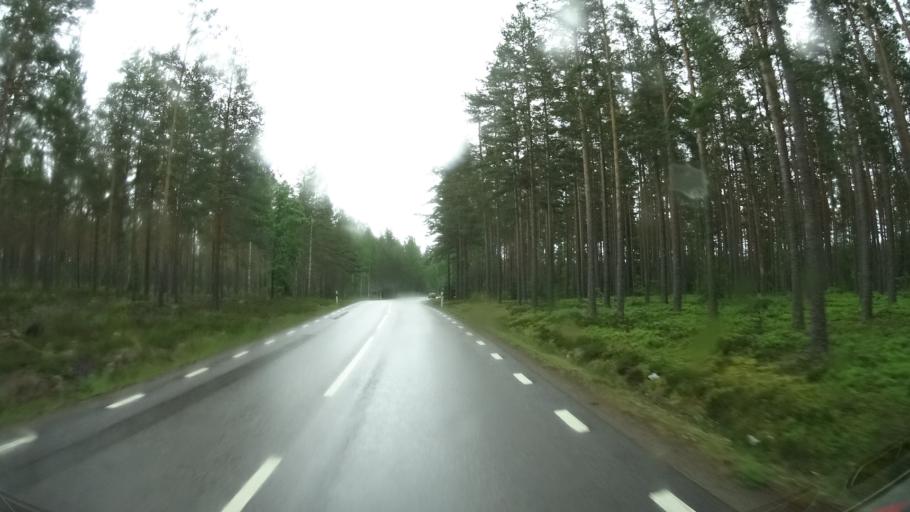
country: SE
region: Kalmar
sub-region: Hultsfreds Kommun
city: Hultsfred
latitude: 57.5179
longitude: 15.8078
